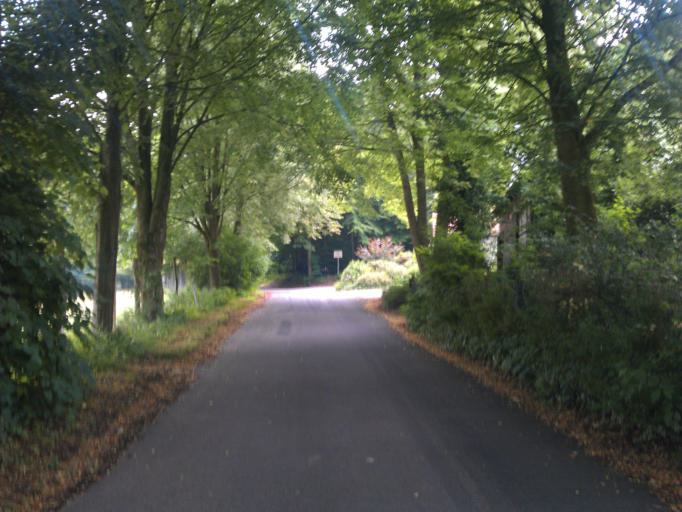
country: DE
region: North Rhine-Westphalia
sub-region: Regierungsbezirk Detmold
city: Lemgo
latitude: 52.0458
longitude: 8.9143
